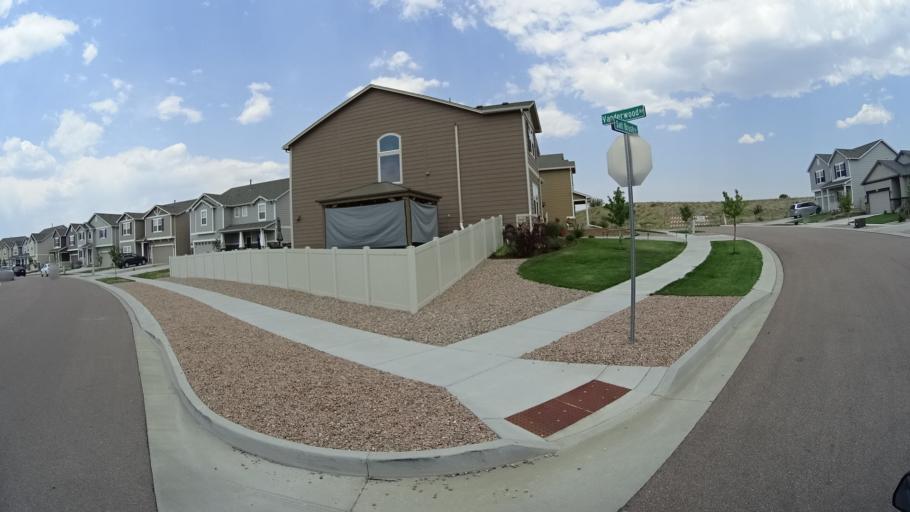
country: US
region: Colorado
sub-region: El Paso County
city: Black Forest
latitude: 38.9543
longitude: -104.6973
